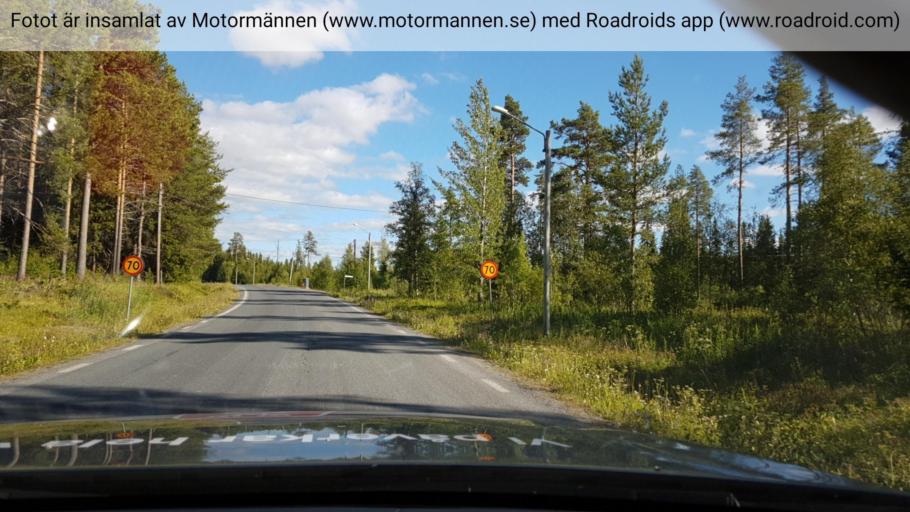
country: SE
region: Jaemtland
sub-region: Krokoms Kommun
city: Valla
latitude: 63.3009
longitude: 13.8343
